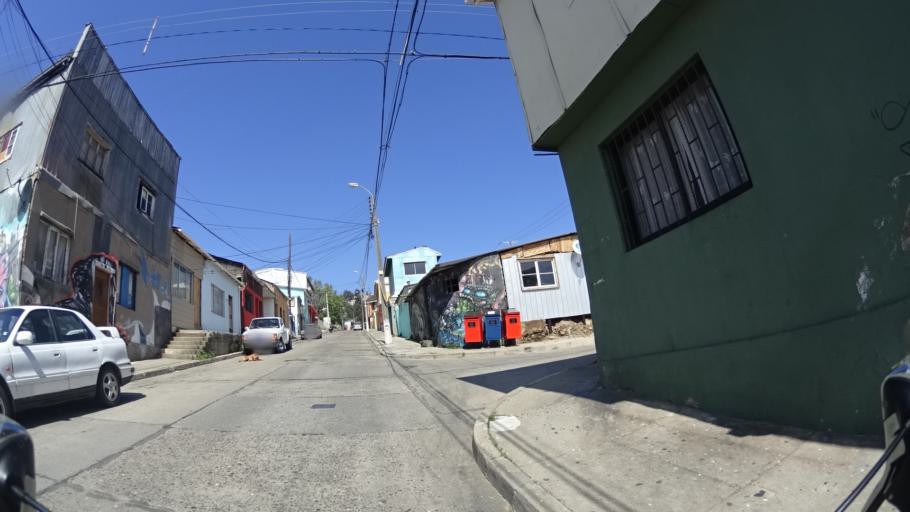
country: CL
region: Valparaiso
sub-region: Provincia de Valparaiso
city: Valparaiso
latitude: -33.0520
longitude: -71.6221
